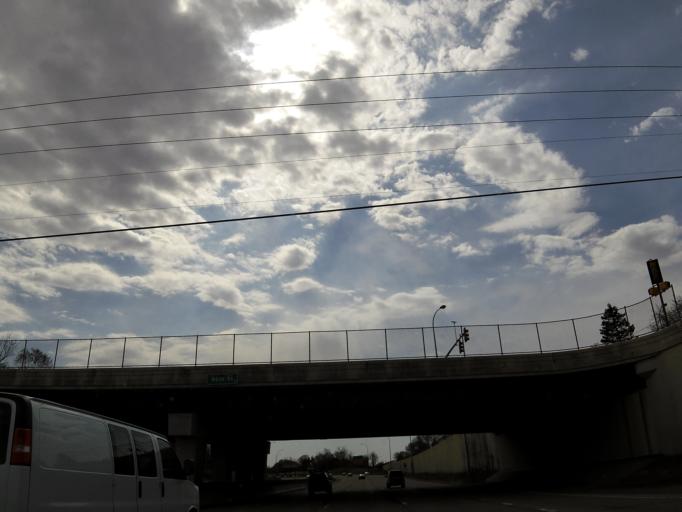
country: US
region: Minnesota
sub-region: Hennepin County
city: Richfield
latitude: 44.8484
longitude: -93.2476
